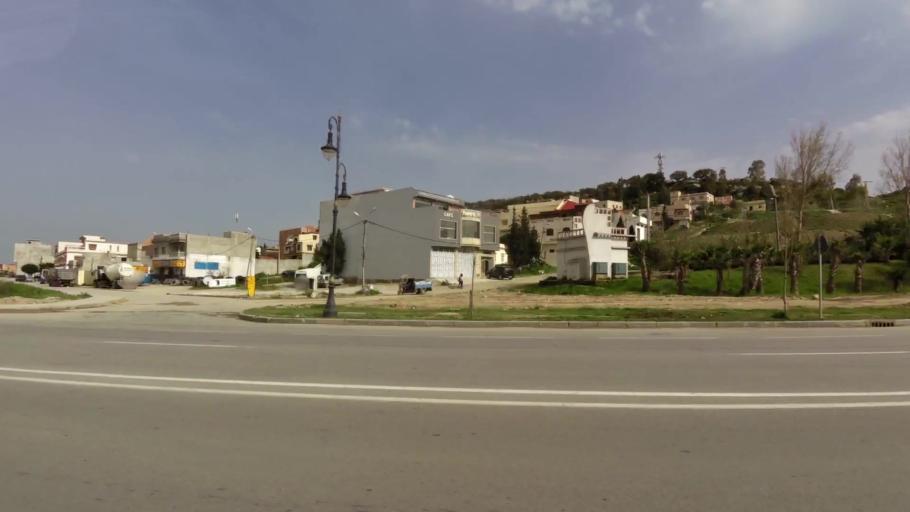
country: MA
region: Tanger-Tetouan
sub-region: Tanger-Assilah
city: Boukhalef
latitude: 35.7012
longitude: -5.9142
